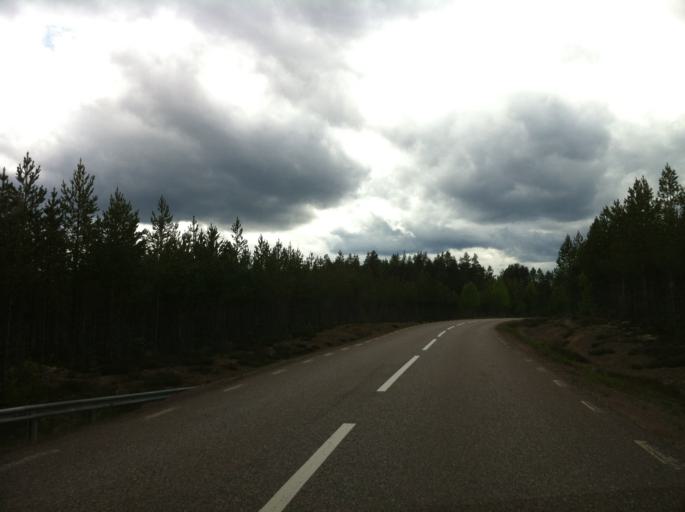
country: NO
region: Hedmark
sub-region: Trysil
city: Innbygda
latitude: 61.4378
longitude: 13.1035
